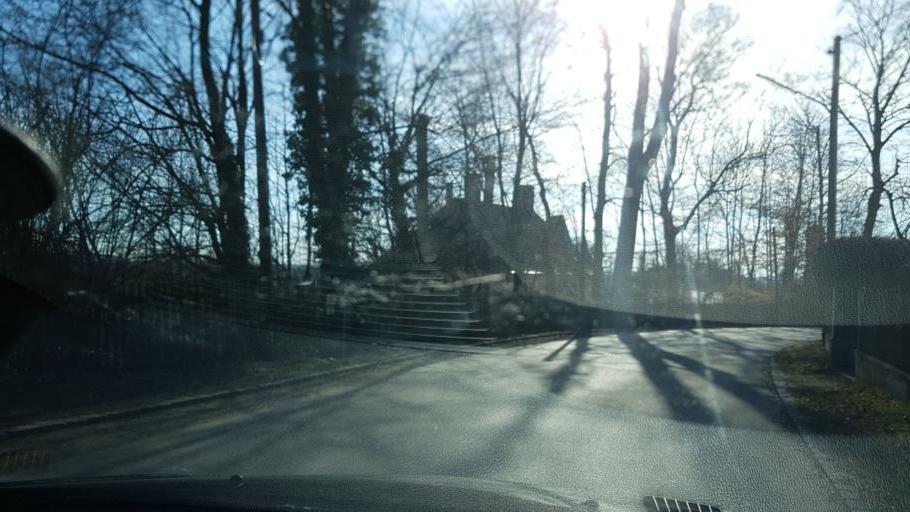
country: DE
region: Bavaria
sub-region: Upper Bavaria
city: Oberschweinbach
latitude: 48.2195
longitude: 11.1756
